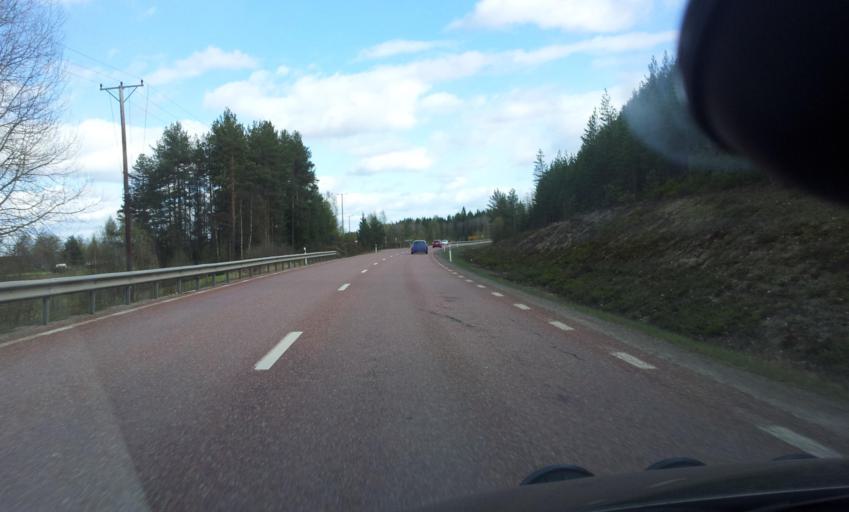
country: SE
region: Gaevleborg
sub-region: Ljusdals Kommun
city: Ljusdal
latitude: 61.8055
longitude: 16.1052
